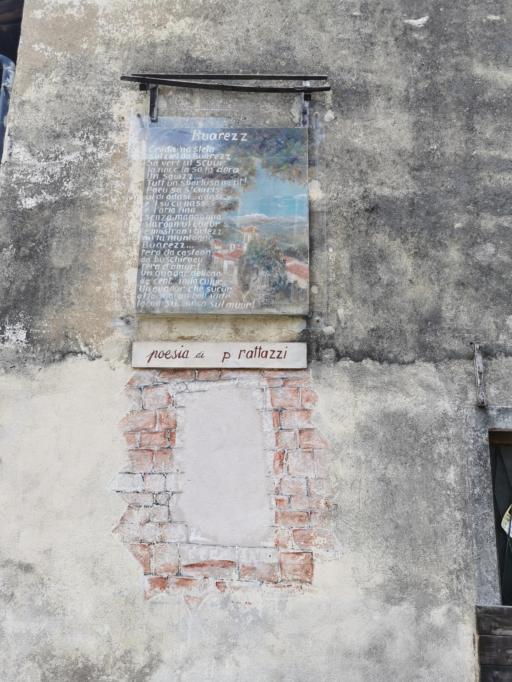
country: IT
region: Lombardy
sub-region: Provincia di Varese
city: Ganna
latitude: 45.9129
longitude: 8.8340
